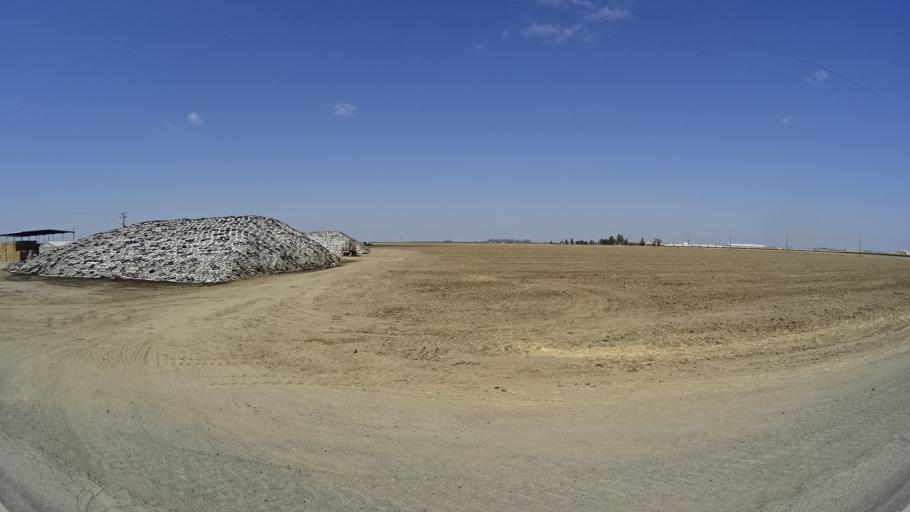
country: US
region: California
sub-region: Kings County
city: Home Garden
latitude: 36.2520
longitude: -119.6369
